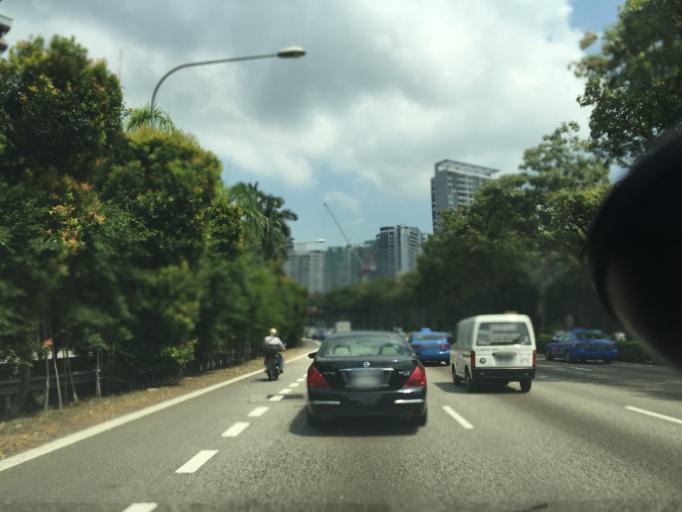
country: SG
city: Singapore
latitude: 1.3173
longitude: 103.8489
